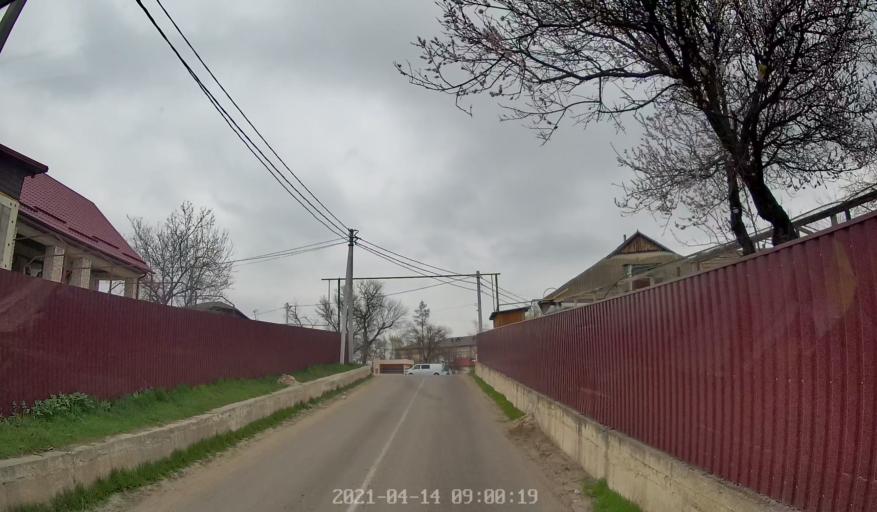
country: MD
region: Chisinau
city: Vadul lui Voda
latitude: 47.0989
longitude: 29.1116
